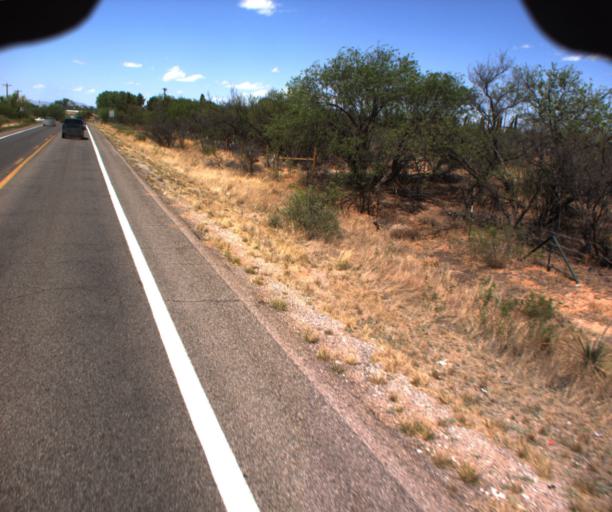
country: US
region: Arizona
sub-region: Cochise County
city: Saint David
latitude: 31.8642
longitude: -110.2058
